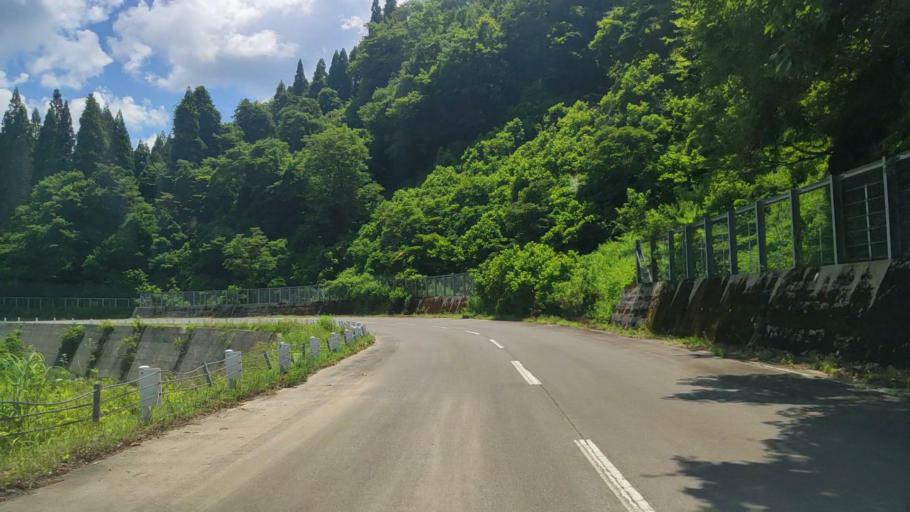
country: JP
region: Fukui
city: Ono
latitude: 35.8303
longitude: 136.4444
